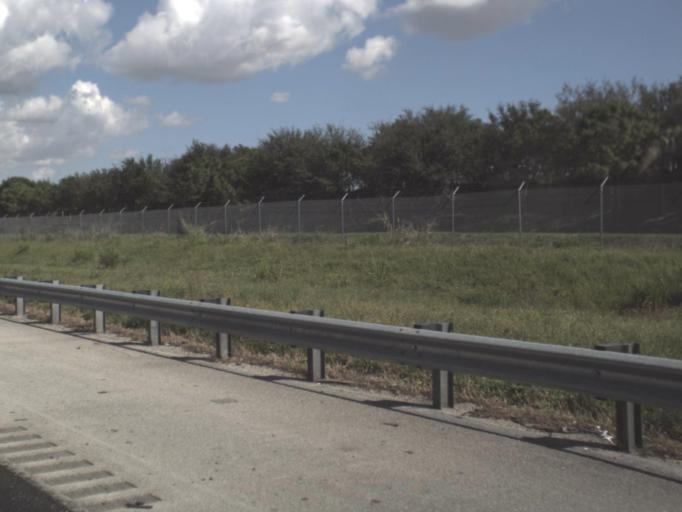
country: US
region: Florida
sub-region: Palm Beach County
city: Villages of Oriole
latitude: 26.4936
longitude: -80.1724
